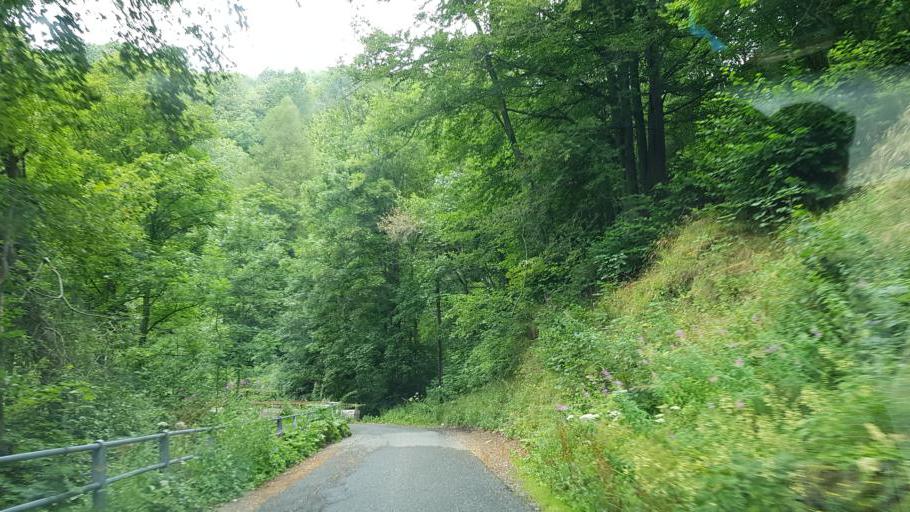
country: IT
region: Piedmont
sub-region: Provincia di Cuneo
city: Stroppo
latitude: 44.5206
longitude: 7.1286
